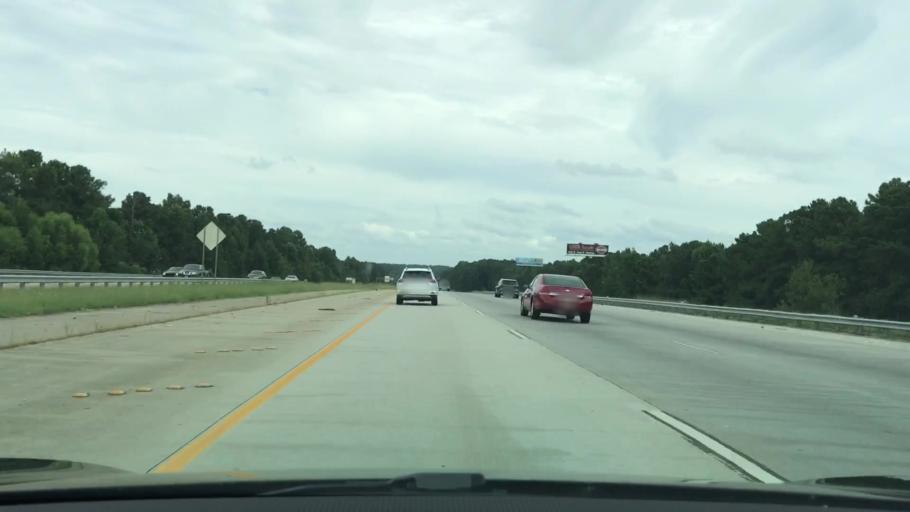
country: US
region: Georgia
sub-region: Coweta County
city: Grantville
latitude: 33.2435
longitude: -84.8064
